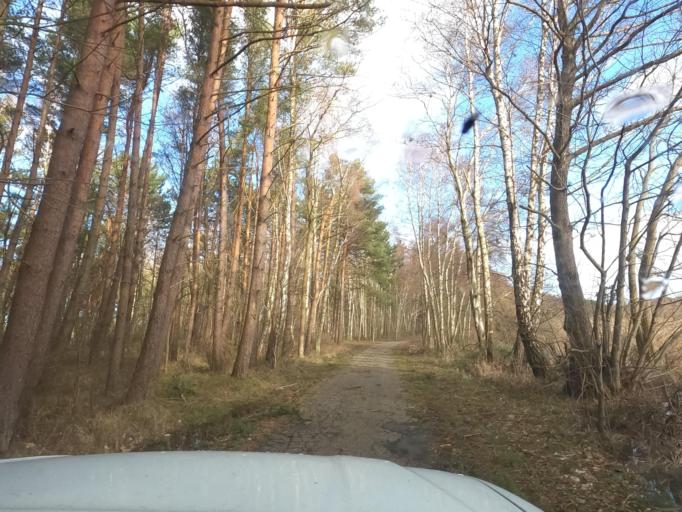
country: PL
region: West Pomeranian Voivodeship
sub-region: Powiat koszalinski
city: Sianow
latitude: 54.3507
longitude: 16.2678
